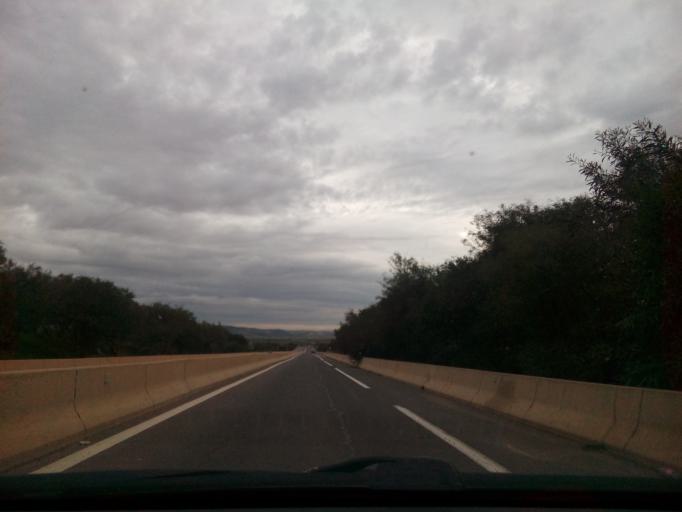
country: DZ
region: Oran
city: Sidi ech Chahmi
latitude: 35.5436
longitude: -0.3785
